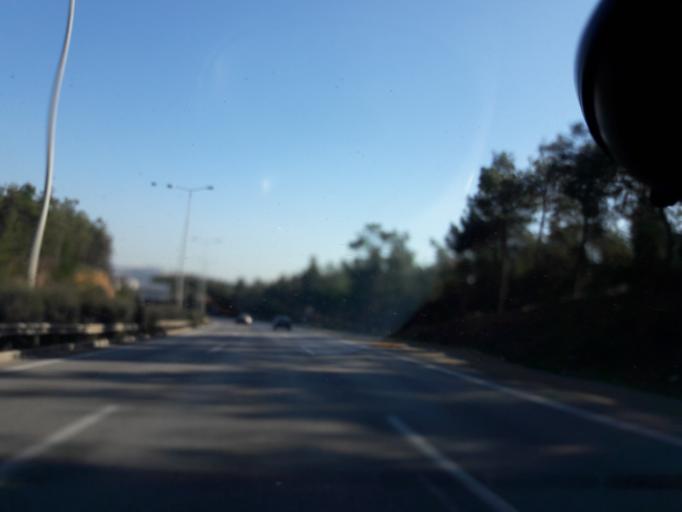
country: GR
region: Central Macedonia
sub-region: Nomos Thessalonikis
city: Triandria
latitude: 40.6160
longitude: 22.9848
